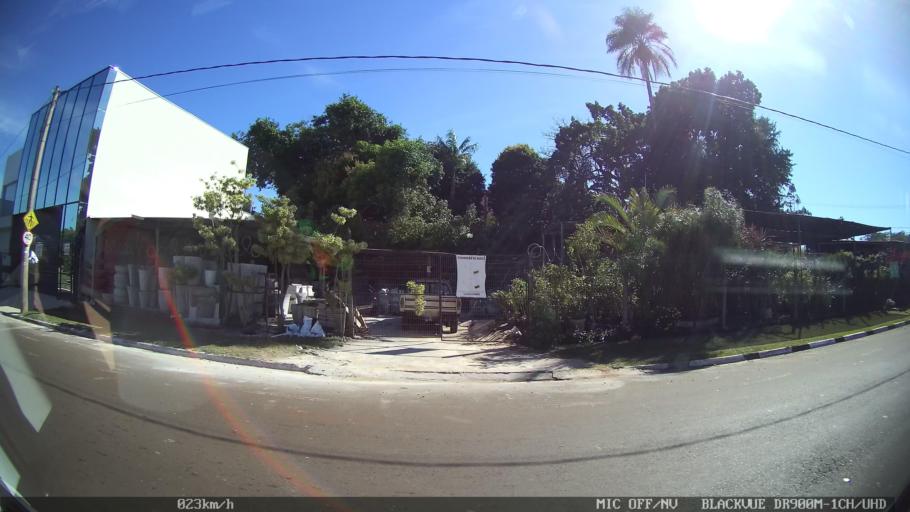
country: BR
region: Sao Paulo
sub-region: Franca
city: Franca
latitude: -20.5206
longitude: -47.3802
